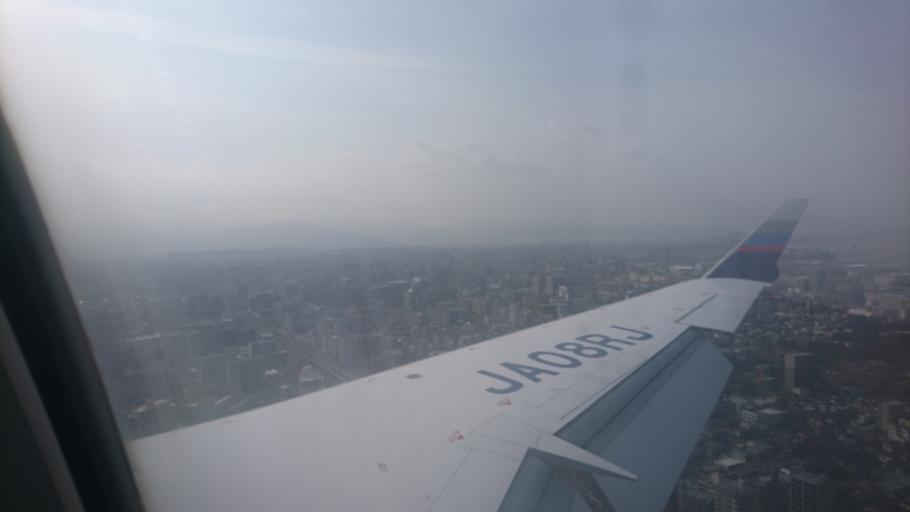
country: JP
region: Fukuoka
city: Fukuoka-shi
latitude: 33.6172
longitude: 130.4289
